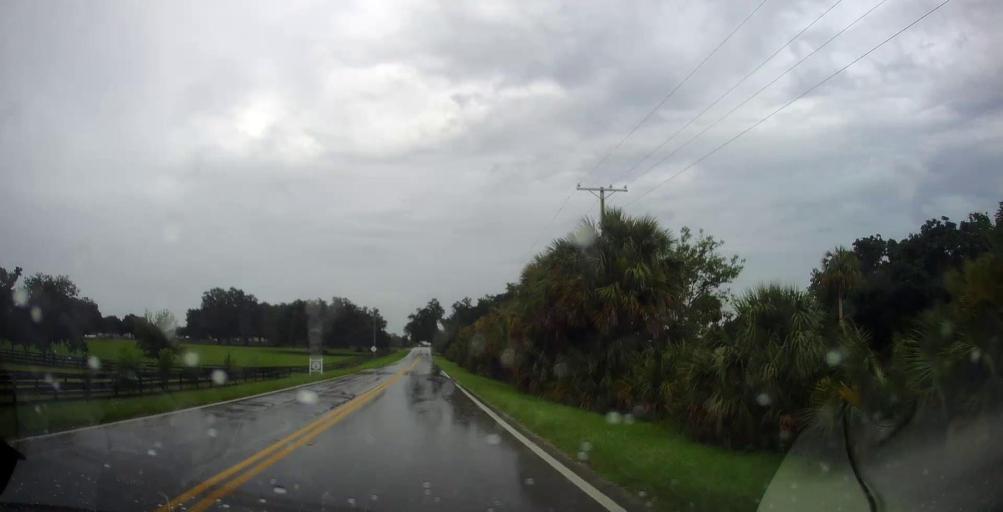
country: US
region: Florida
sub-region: Marion County
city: Citra
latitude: 29.3302
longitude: -82.2043
